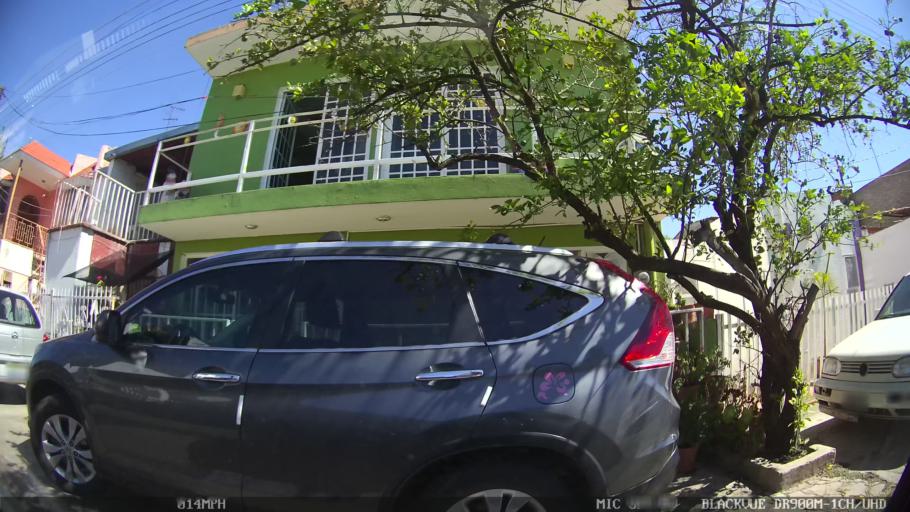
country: MX
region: Jalisco
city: Tlaquepaque
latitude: 20.6481
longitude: -103.2973
